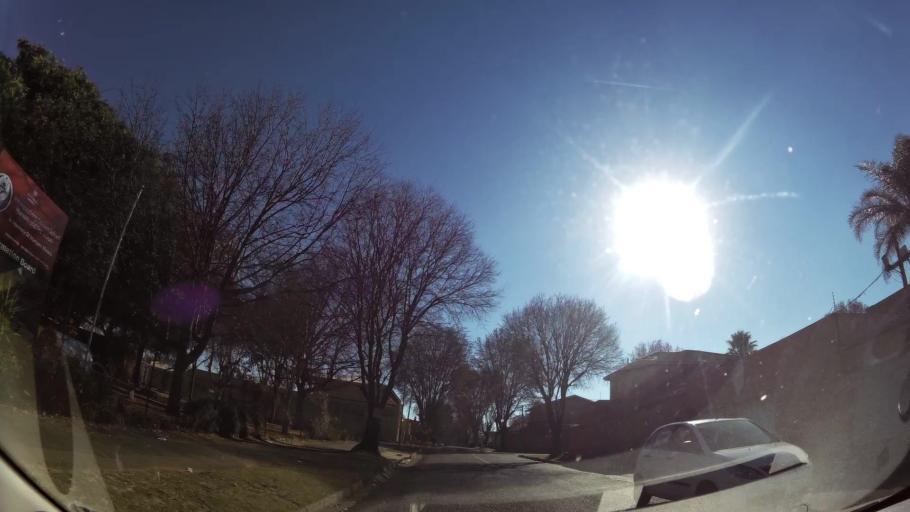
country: ZA
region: Gauteng
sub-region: City of Johannesburg Metropolitan Municipality
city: Johannesburg
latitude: -26.2016
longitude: 28.0101
